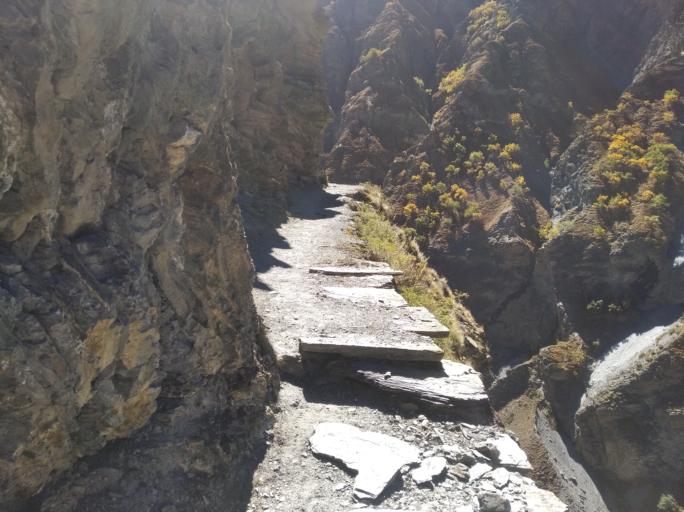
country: NP
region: Western Region
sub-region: Dhawalagiri Zone
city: Jomsom
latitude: 28.8447
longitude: 83.3562
